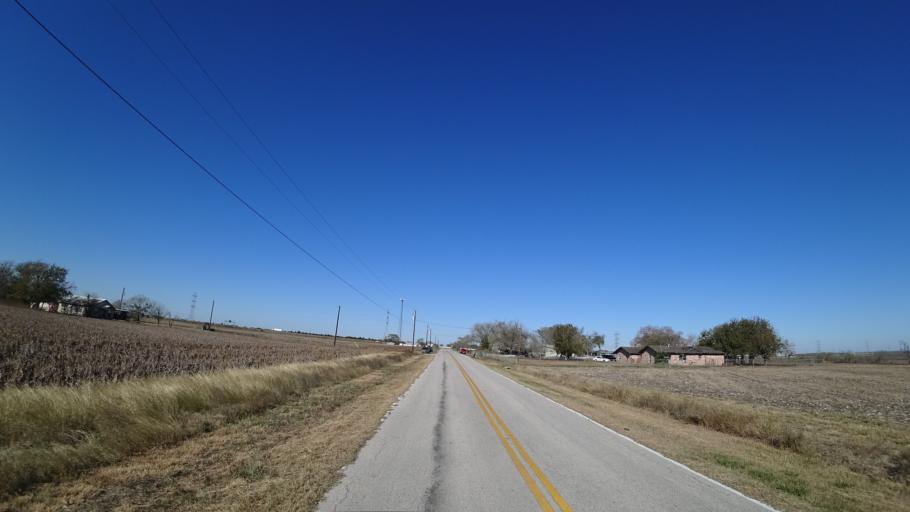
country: US
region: Texas
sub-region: Travis County
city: Onion Creek
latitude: 30.0986
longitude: -97.6642
